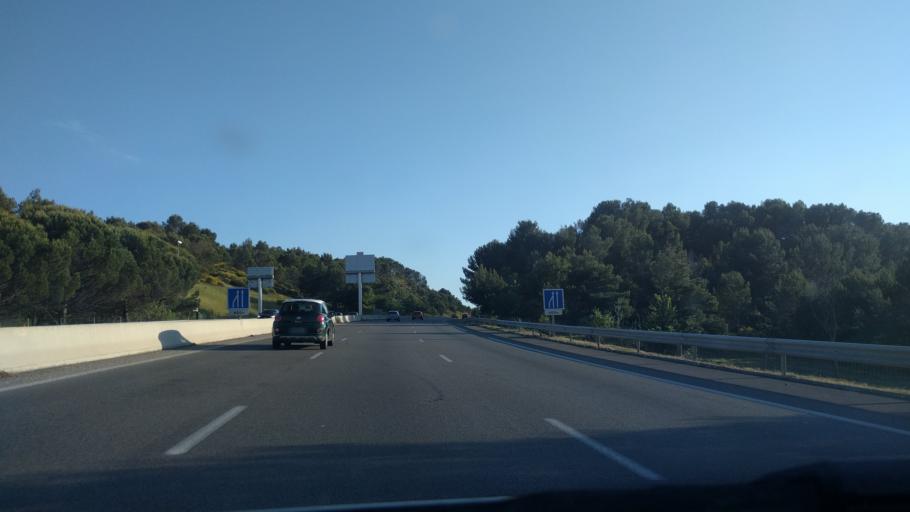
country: FR
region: Provence-Alpes-Cote d'Azur
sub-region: Departement des Bouches-du-Rhone
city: Venelles
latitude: 43.6011
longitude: 5.4954
